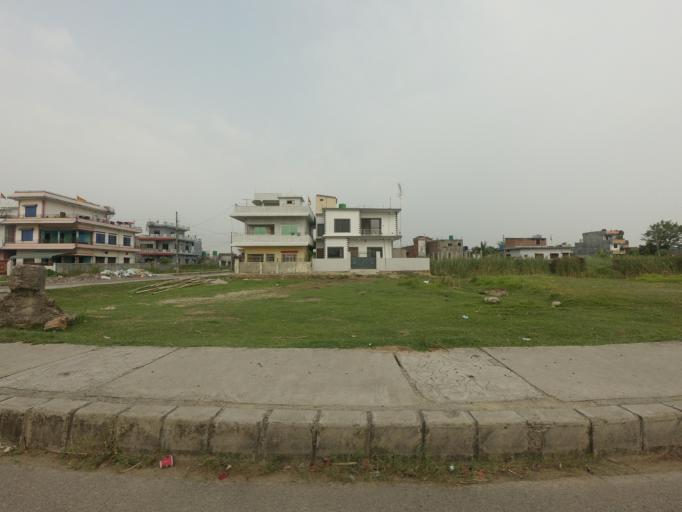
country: NP
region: Western Region
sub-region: Lumbini Zone
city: Bhairahawa
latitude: 27.4971
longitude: 83.4524
